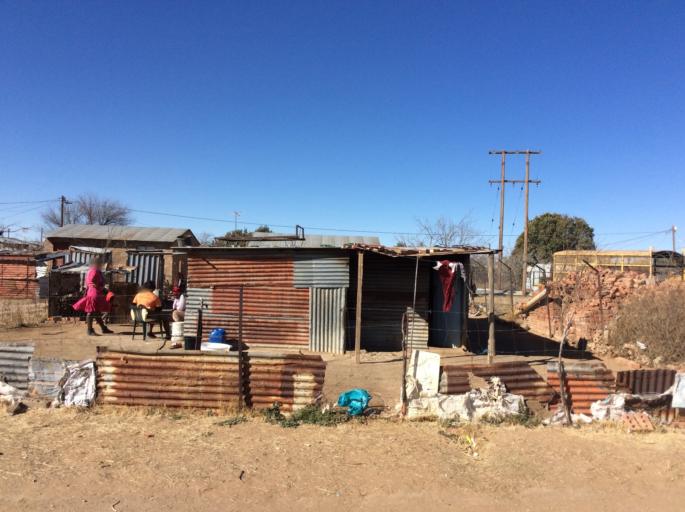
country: ZA
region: Orange Free State
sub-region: Lejweleputswa District Municipality
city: Brandfort
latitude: -28.7355
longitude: 26.1044
